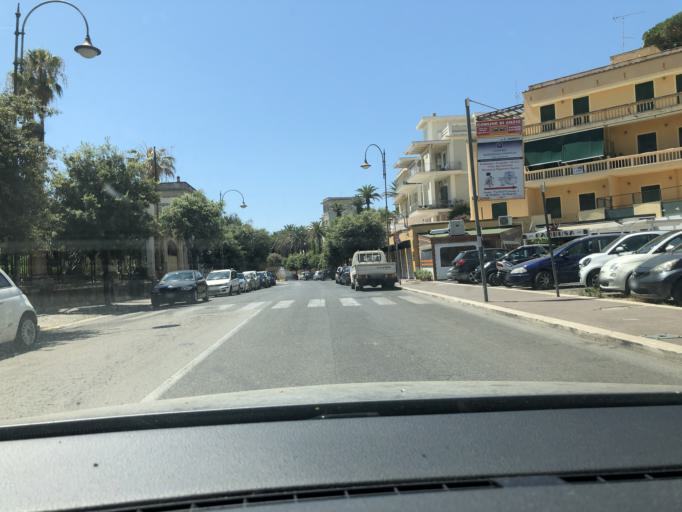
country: IT
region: Latium
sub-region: Citta metropolitana di Roma Capitale
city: Anzio
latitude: 41.4521
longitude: 12.6348
